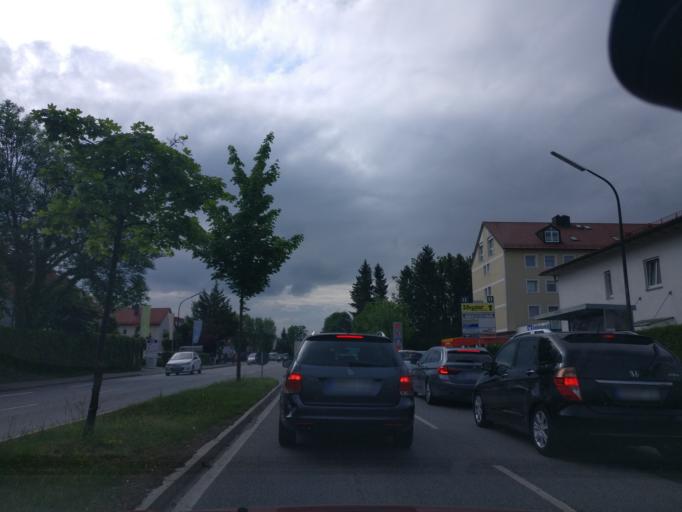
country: DE
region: Bavaria
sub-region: Upper Bavaria
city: Karlsfeld
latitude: 48.2229
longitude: 11.4719
